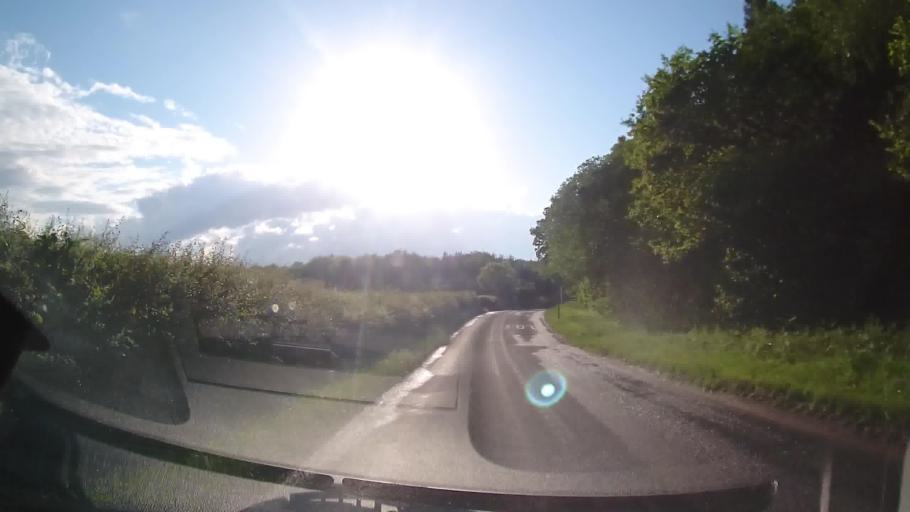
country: GB
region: England
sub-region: Leicestershire
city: Kirby Muxloe
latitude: 52.6542
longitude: -1.2546
